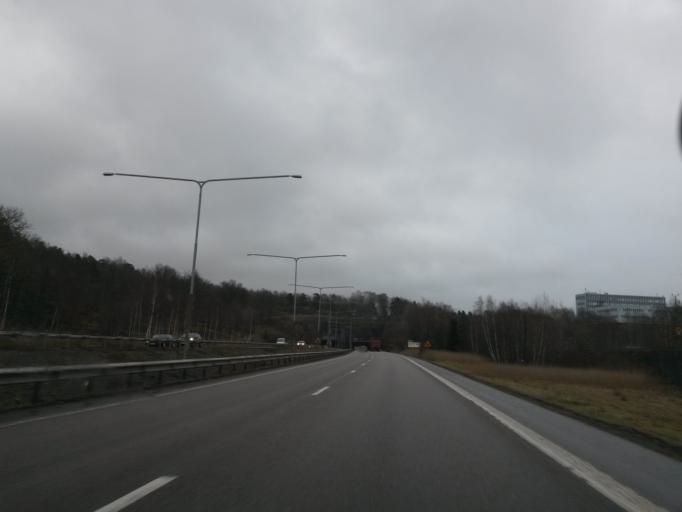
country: SE
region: Vaestra Goetaland
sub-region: Uddevalla Kommun
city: Uddevalla
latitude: 58.3528
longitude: 11.8887
